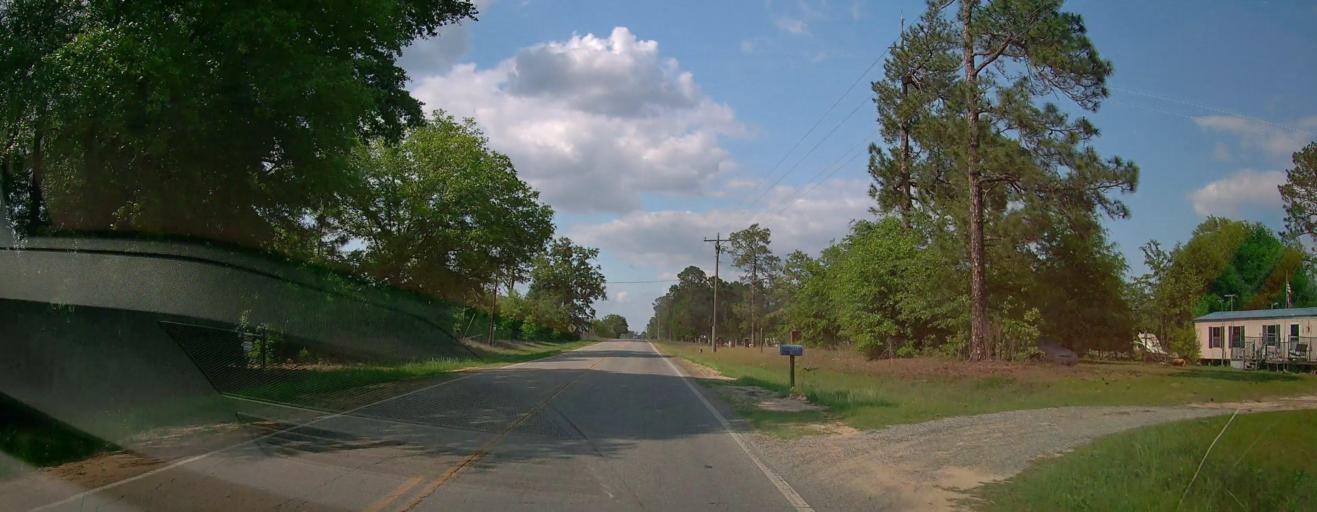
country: US
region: Georgia
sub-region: Laurens County
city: East Dublin
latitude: 32.5842
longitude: -82.8643
